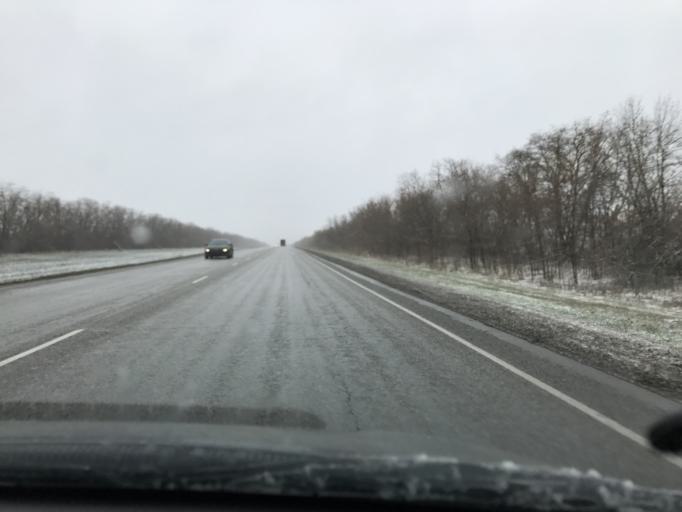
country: RU
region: Rostov
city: Mechetinskaya
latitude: 46.7414
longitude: 40.4696
